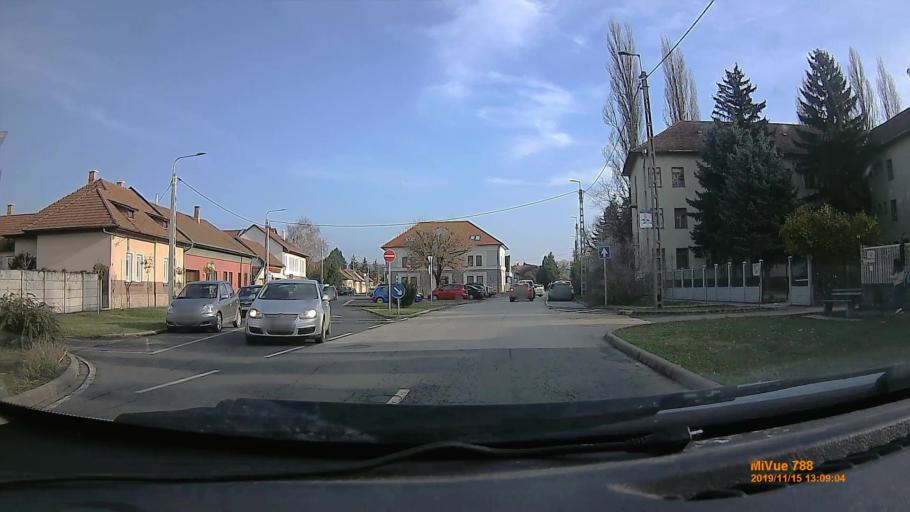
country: HU
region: Bekes
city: Gyula
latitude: 46.6428
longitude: 21.2756
